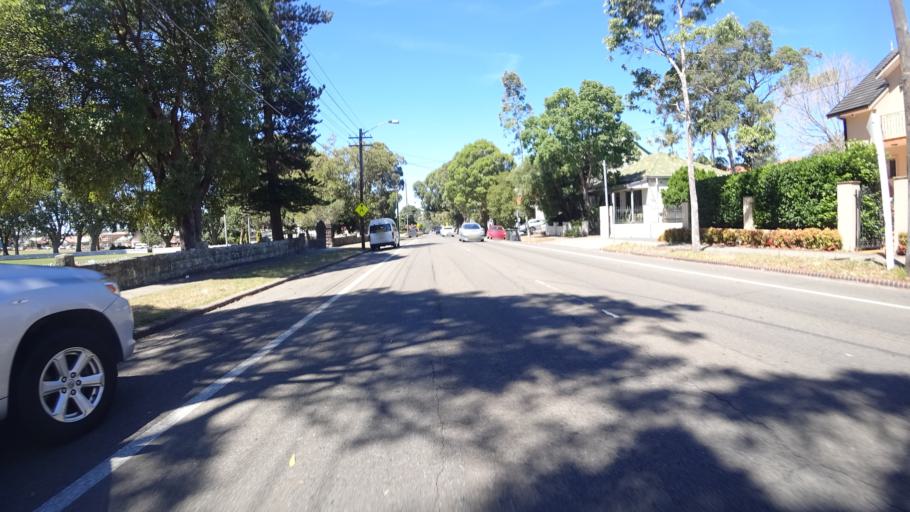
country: AU
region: New South Wales
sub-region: Rockdale
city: Arncliffe
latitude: -33.9362
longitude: 151.1428
